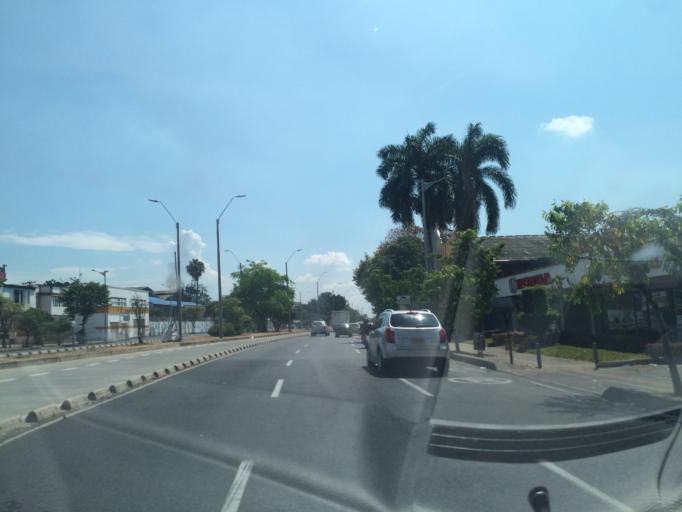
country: CO
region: Valle del Cauca
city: Cali
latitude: 3.4707
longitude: -76.5097
